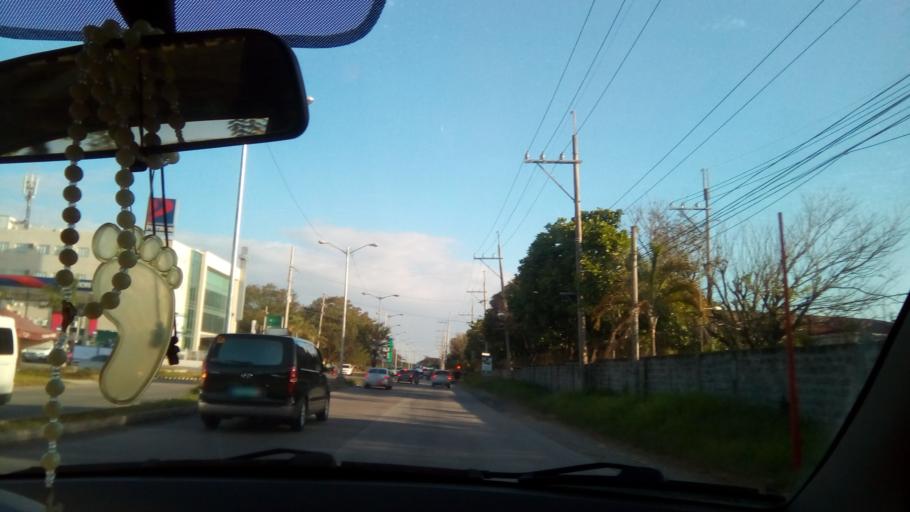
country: PH
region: Calabarzon
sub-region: Province of Laguna
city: San Pedro
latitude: 14.3988
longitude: 121.0118
